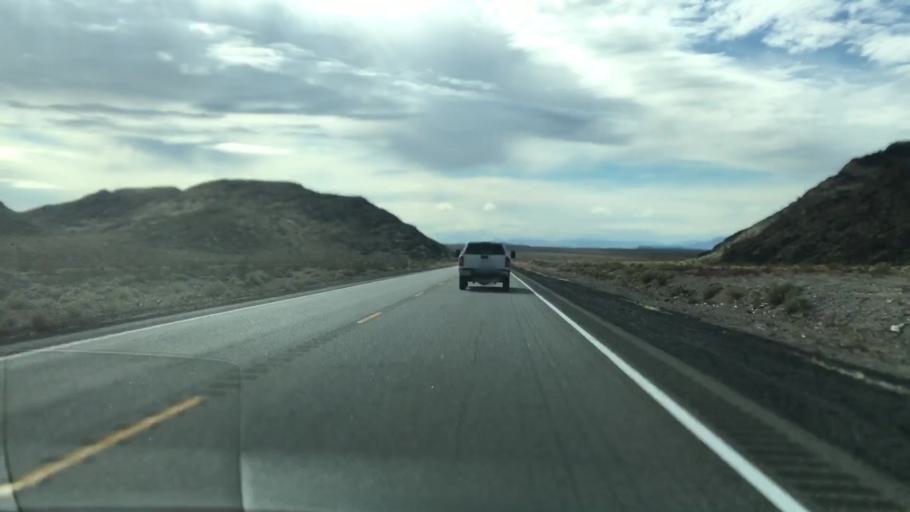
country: US
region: Nevada
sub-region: Nye County
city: Pahrump
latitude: 36.5700
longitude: -116.0788
